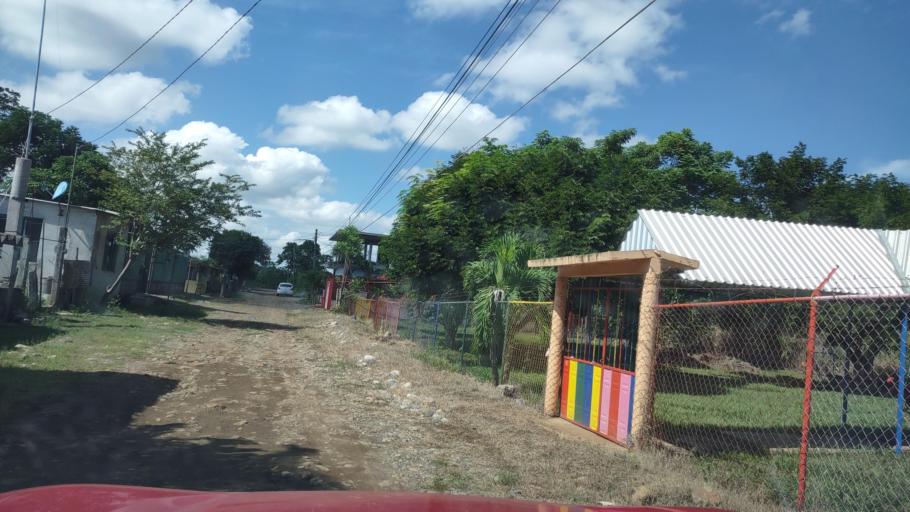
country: MX
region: Veracruz
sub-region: Martinez de la Torre
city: La Union Paso Largo
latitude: 20.1303
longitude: -96.9973
